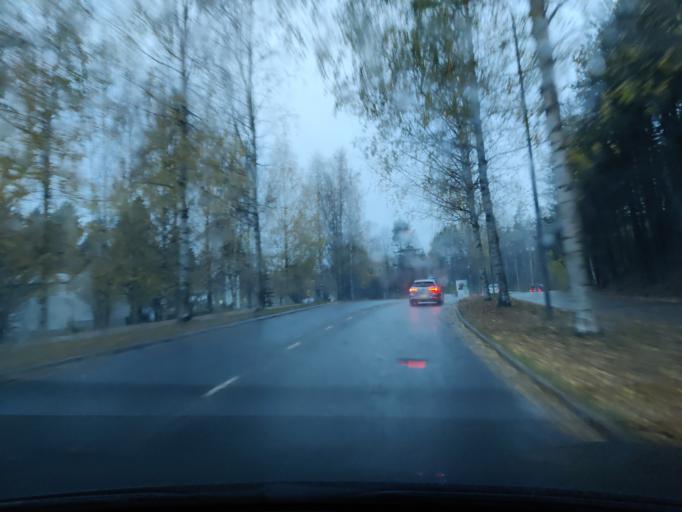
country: FI
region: Northern Savo
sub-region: Kuopio
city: Kuopio
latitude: 62.8478
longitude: 27.6434
